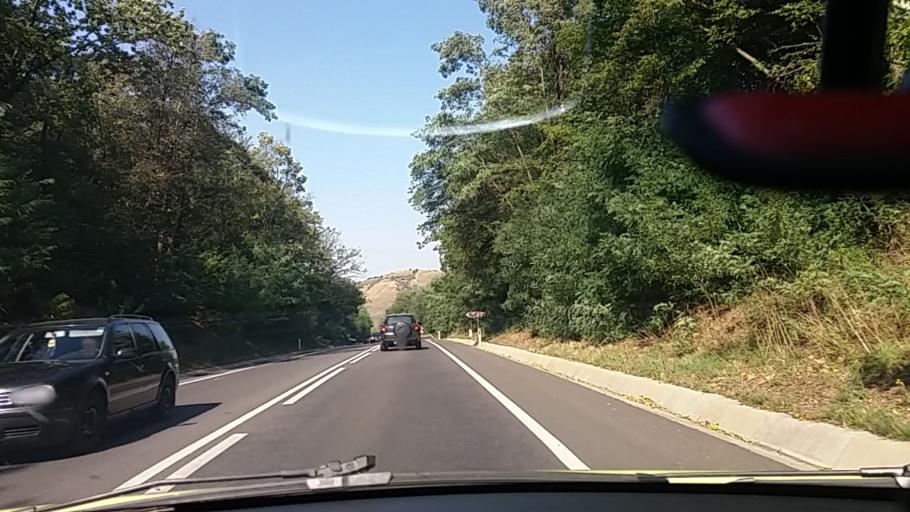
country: RO
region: Sibiu
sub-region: Comuna Slimnic
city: Slimnic
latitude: 45.8877
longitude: 24.1641
